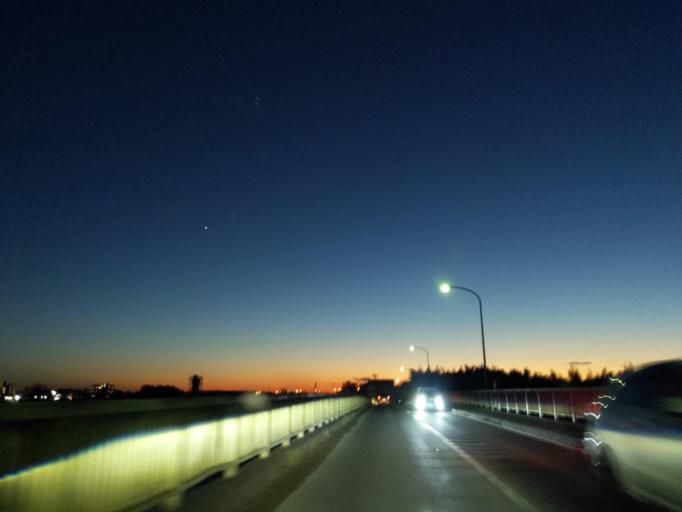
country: JP
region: Fukushima
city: Sukagawa
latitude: 37.3075
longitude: 140.3812
